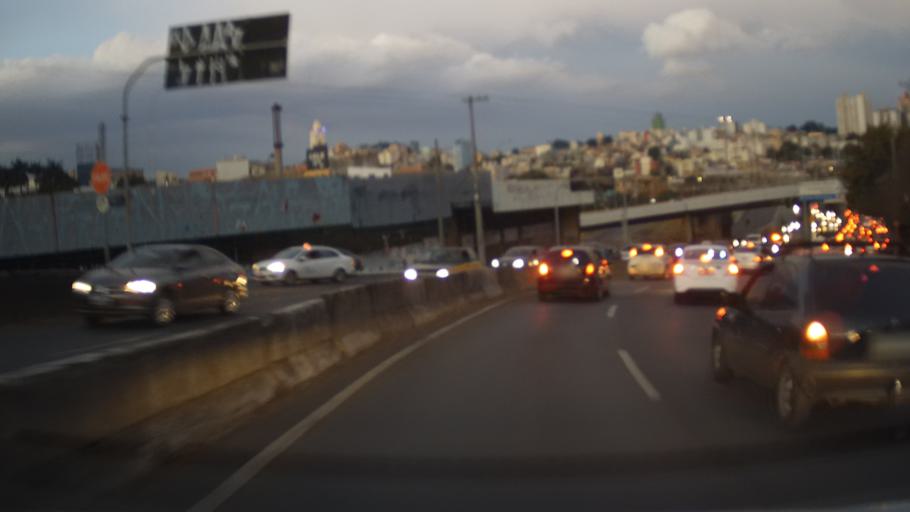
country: BR
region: Minas Gerais
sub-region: Belo Horizonte
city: Belo Horizonte
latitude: -19.9139
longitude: -43.9444
